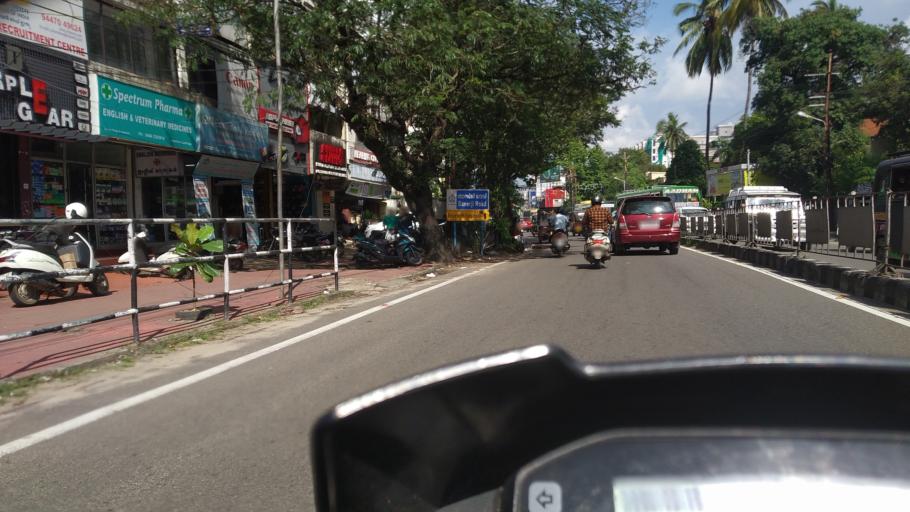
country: IN
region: Kerala
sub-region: Ernakulam
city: Cochin
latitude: 9.9853
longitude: 76.2791
